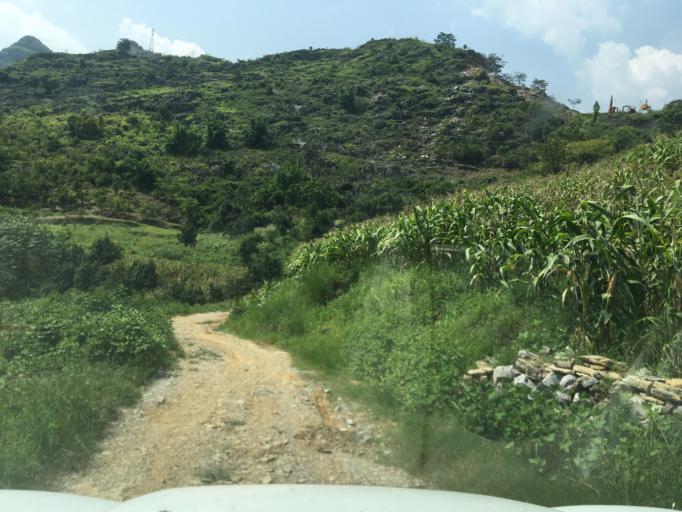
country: CN
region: Guangxi Zhuangzu Zizhiqu
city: Xinzhou
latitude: 24.9955
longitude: 105.7519
